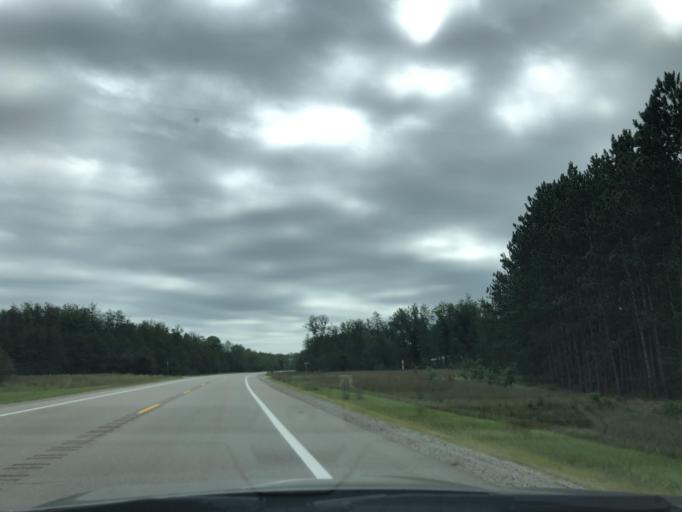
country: US
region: Michigan
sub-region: Clare County
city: Harrison
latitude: 44.0430
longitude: -85.0444
